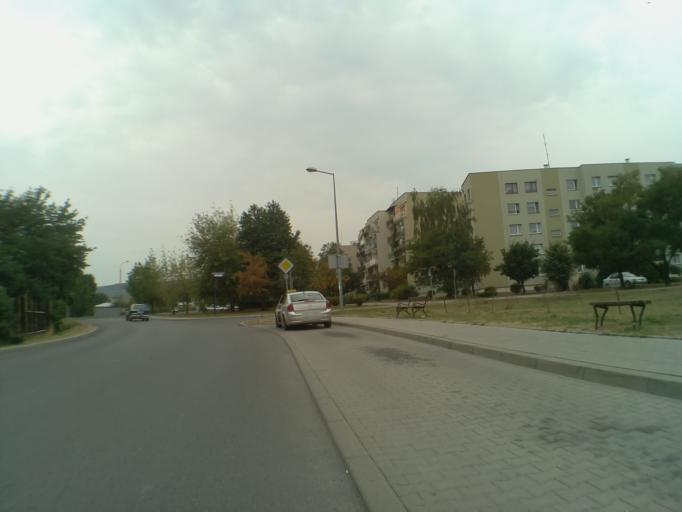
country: PL
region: Lower Silesian Voivodeship
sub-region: Powiat swidnicki
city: Swiebodzice
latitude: 50.8637
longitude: 16.3171
